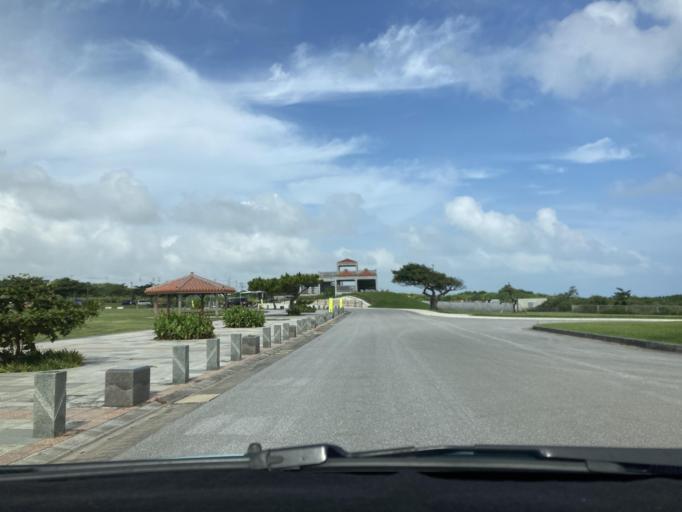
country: JP
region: Okinawa
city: Itoman
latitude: 26.0975
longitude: 127.7262
